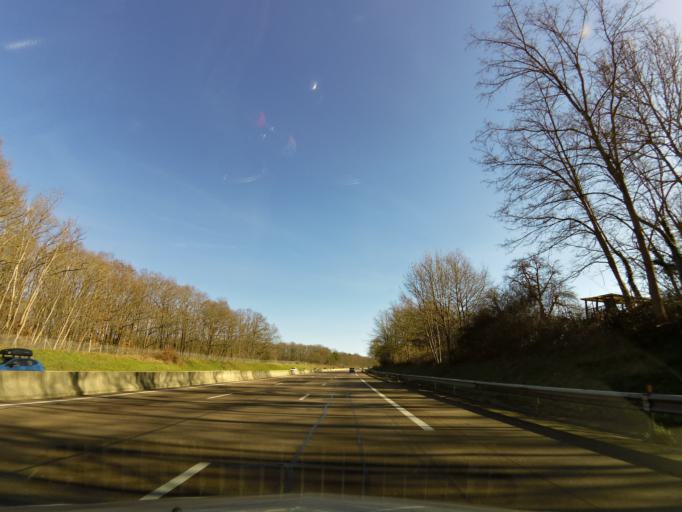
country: FR
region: Bourgogne
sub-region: Departement de l'Yonne
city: Moneteau
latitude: 47.8561
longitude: 3.5828
